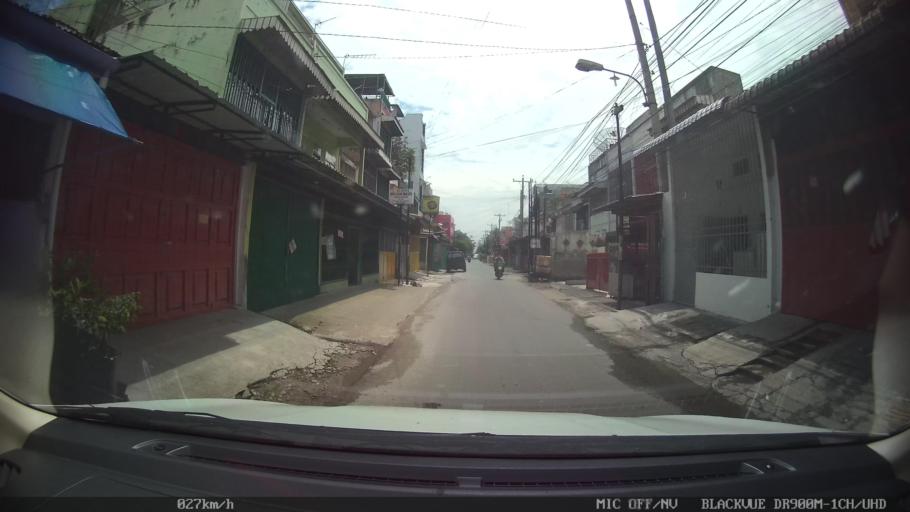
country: ID
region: North Sumatra
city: Medan
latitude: 3.5874
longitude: 98.7093
